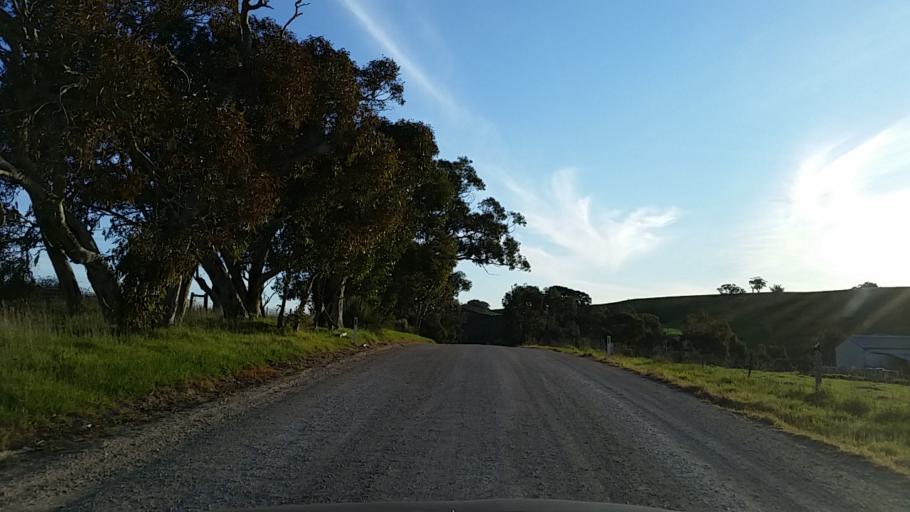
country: AU
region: South Australia
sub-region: Alexandrina
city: Mount Compass
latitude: -35.2852
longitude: 138.6946
